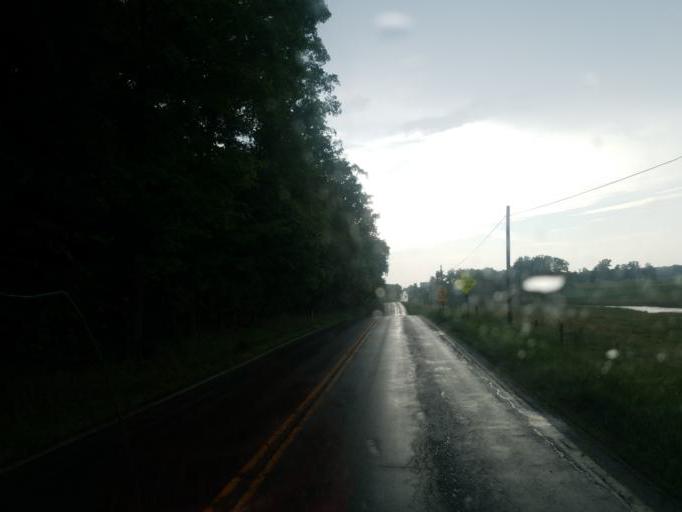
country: US
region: Ohio
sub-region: Wayne County
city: Creston
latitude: 40.9456
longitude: -81.8855
